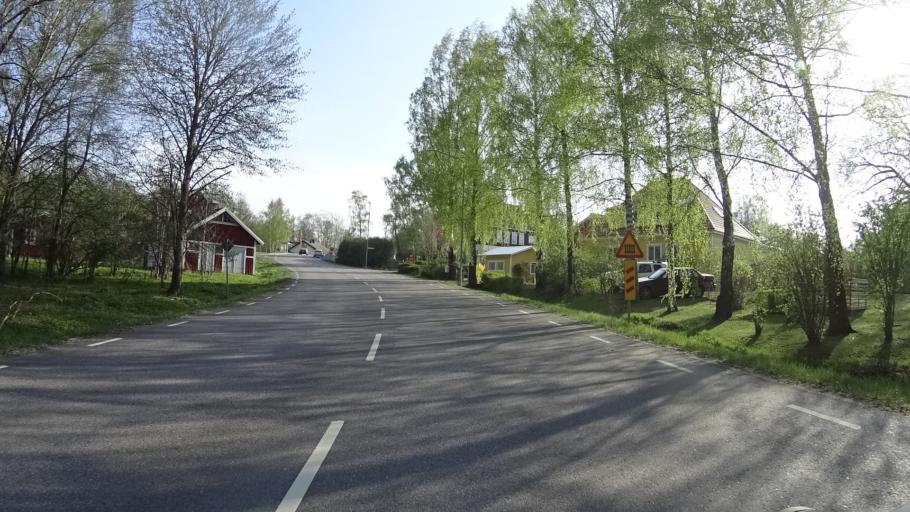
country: SE
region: Vaestra Goetaland
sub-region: Gotene Kommun
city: Goetene
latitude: 58.6315
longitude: 13.4346
